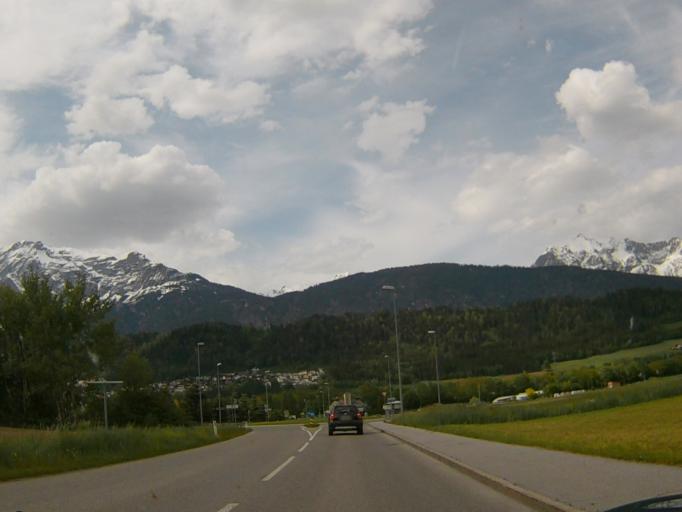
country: AT
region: Tyrol
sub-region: Politischer Bezirk Innsbruck Land
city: Wattenberg
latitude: 47.2950
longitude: 11.6054
